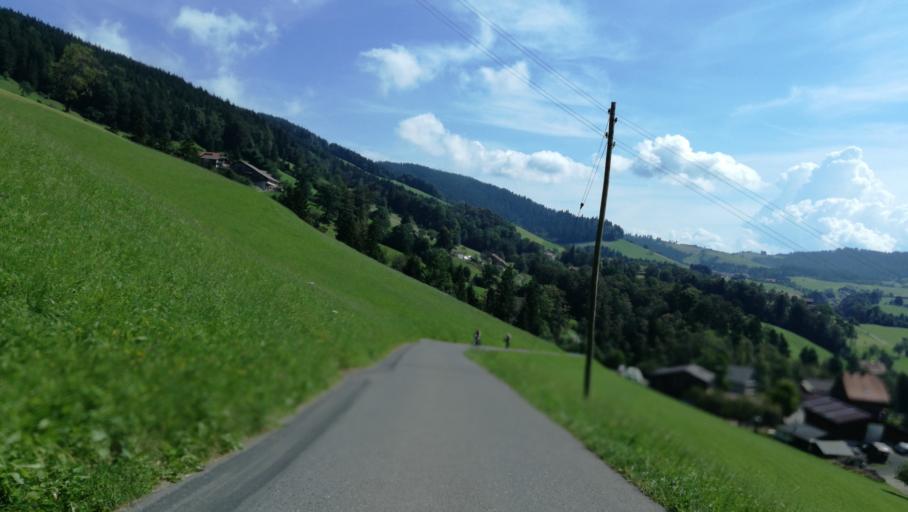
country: CH
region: Zug
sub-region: Zug
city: Unterageri
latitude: 47.1434
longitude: 8.6048
